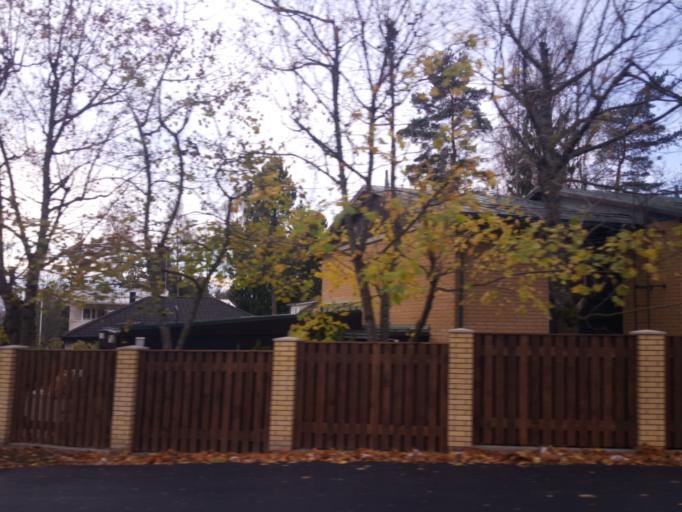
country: FI
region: Uusimaa
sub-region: Helsinki
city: Otaniemi
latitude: 60.2045
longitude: 24.8113
